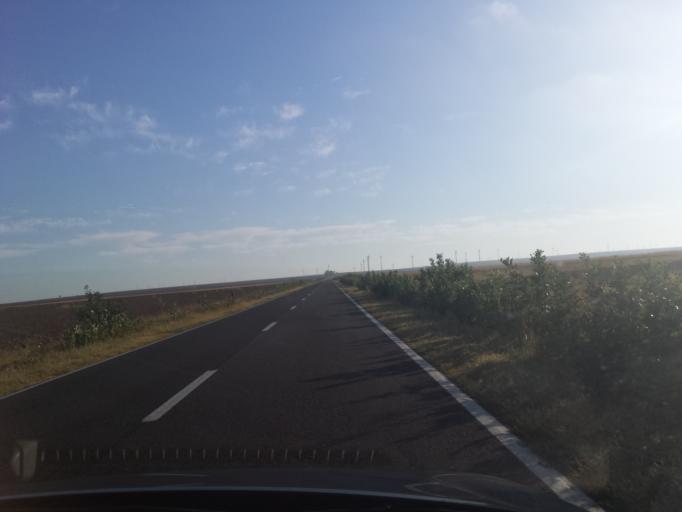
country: RO
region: Constanta
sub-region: Comuna Saraiu
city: Saraiu
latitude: 44.7454
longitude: 28.1825
